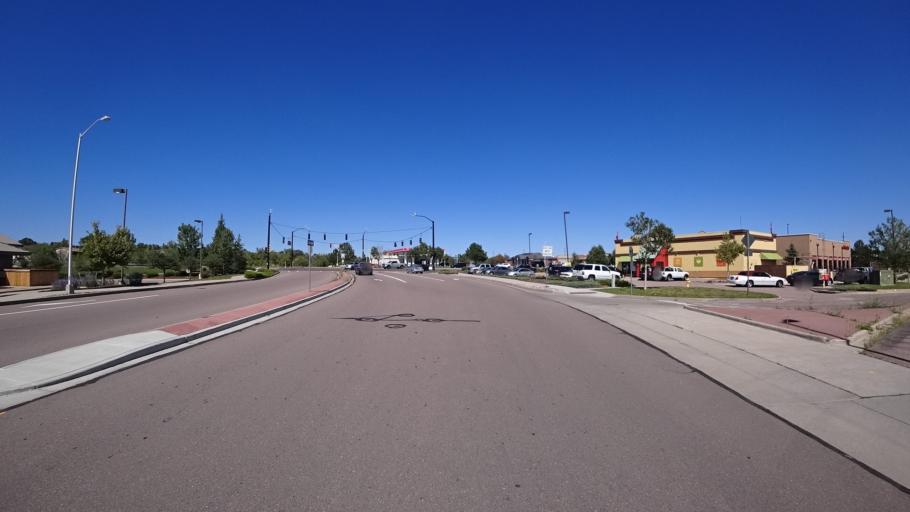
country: US
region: Colorado
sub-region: El Paso County
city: Cimarron Hills
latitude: 38.8563
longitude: -104.7232
